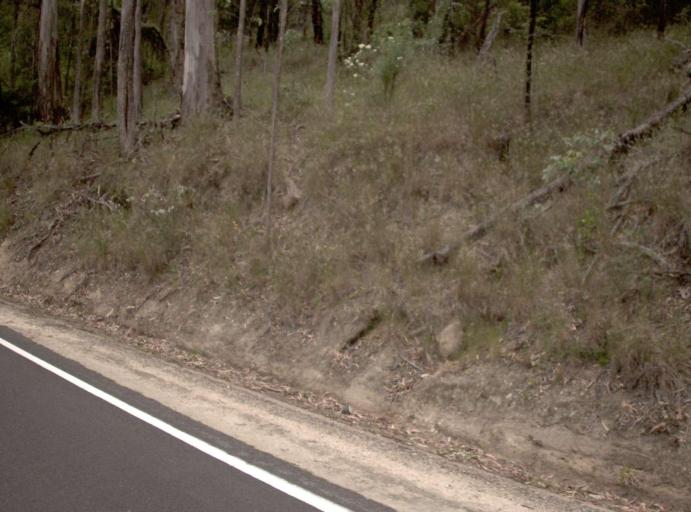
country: AU
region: New South Wales
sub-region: Bombala
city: Bombala
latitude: -37.4530
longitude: 149.1920
